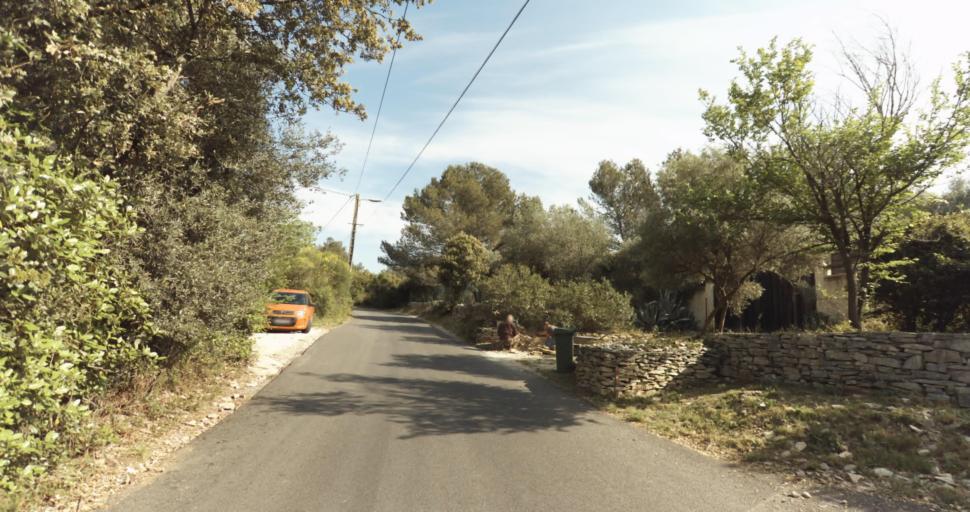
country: FR
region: Languedoc-Roussillon
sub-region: Departement du Gard
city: Poulx
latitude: 43.8734
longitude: 4.3934
